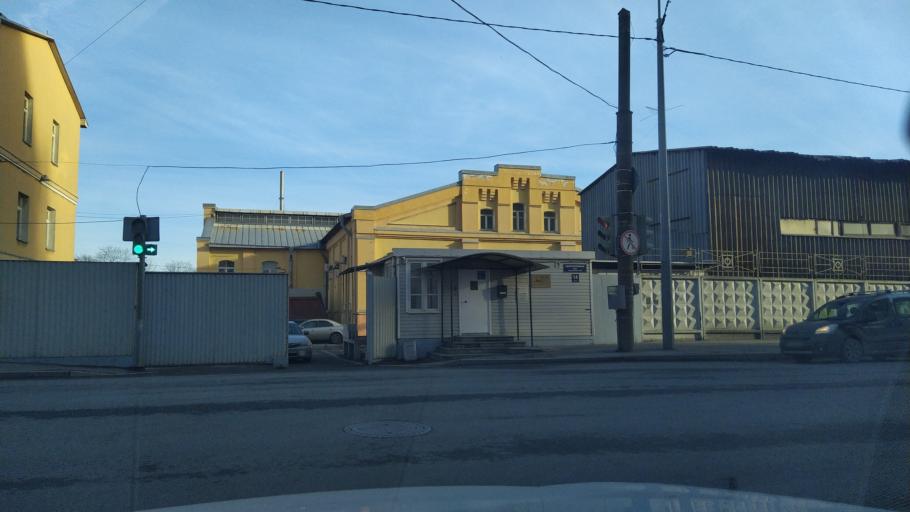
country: RU
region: St.-Petersburg
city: Centralniy
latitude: 59.9105
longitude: 30.3574
